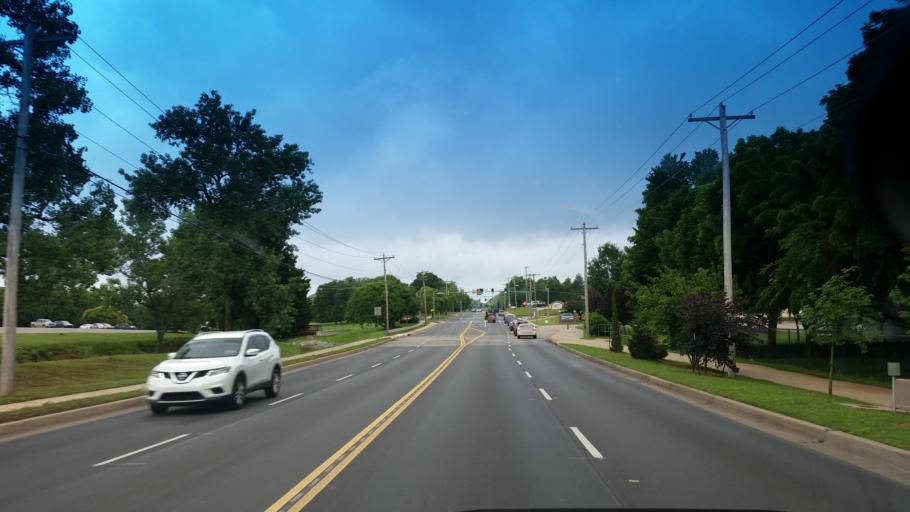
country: US
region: Oklahoma
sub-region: Oklahoma County
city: Edmond
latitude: 35.6472
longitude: -97.4605
